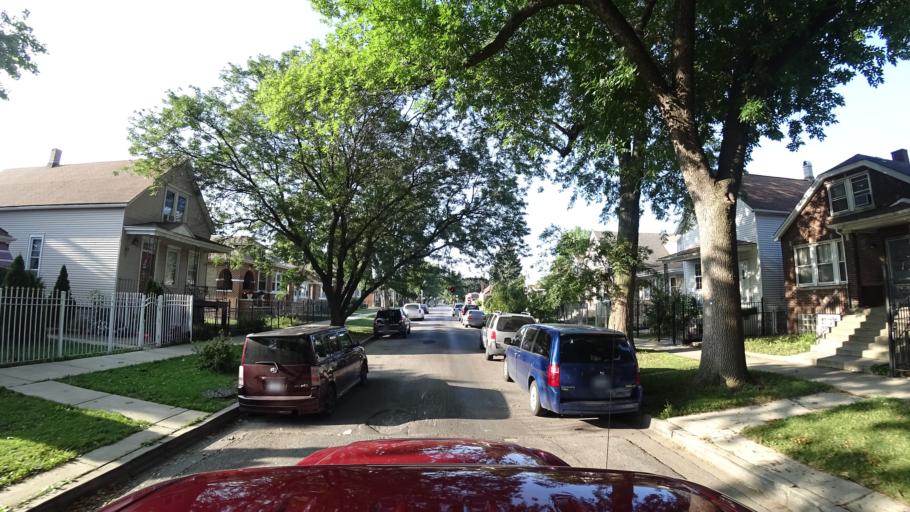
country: US
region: Illinois
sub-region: Cook County
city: Cicero
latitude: 41.7978
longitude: -87.7086
